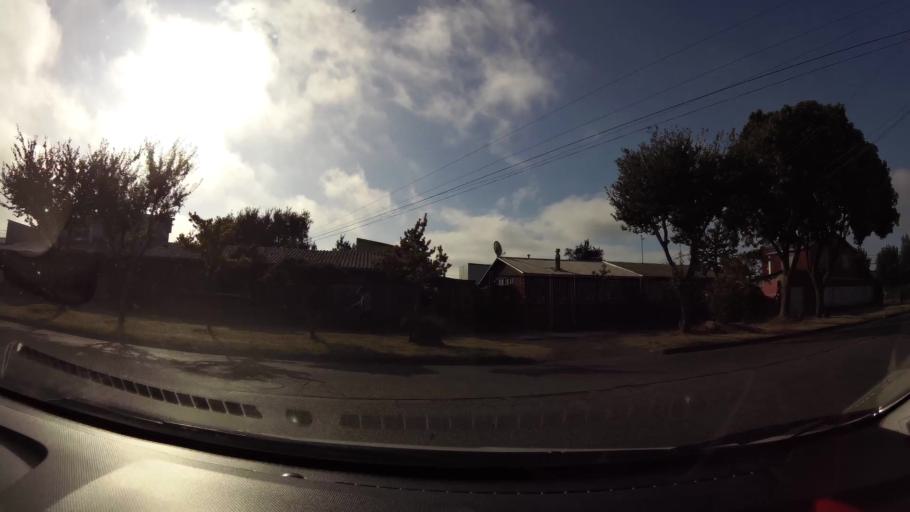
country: CL
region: Biobio
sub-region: Provincia de Concepcion
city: Concepcion
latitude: -36.7920
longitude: -73.1036
